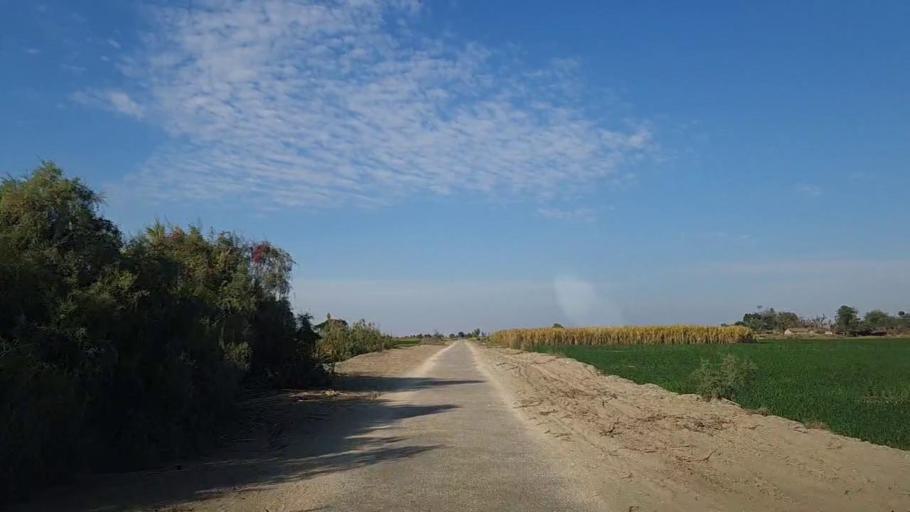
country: PK
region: Sindh
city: Khadro
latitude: 26.3033
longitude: 68.8343
